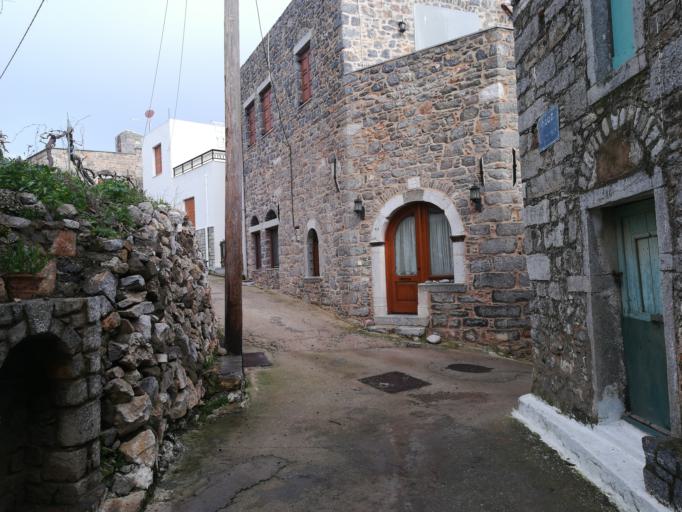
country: GR
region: North Aegean
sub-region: Chios
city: Thymiana
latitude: 38.2479
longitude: 25.9436
